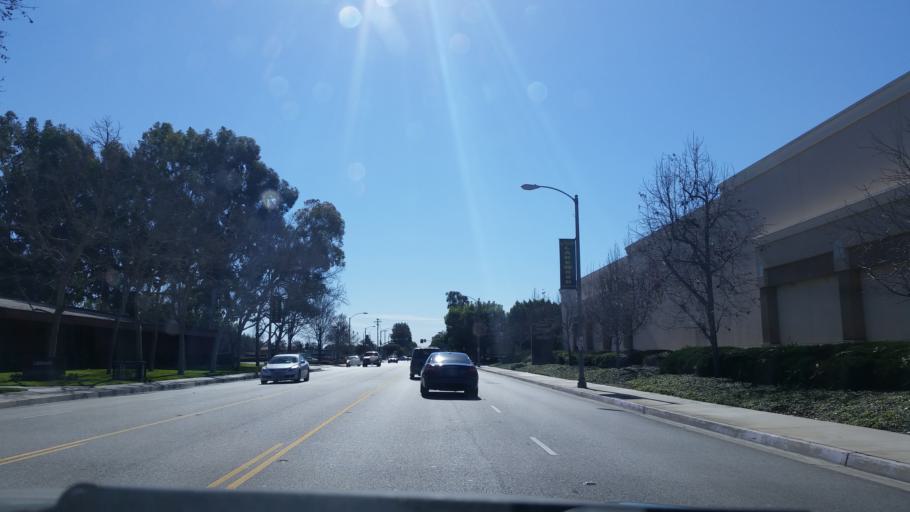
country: US
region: California
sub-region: Los Angeles County
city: Lakewood
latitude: 33.8495
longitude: -118.1338
